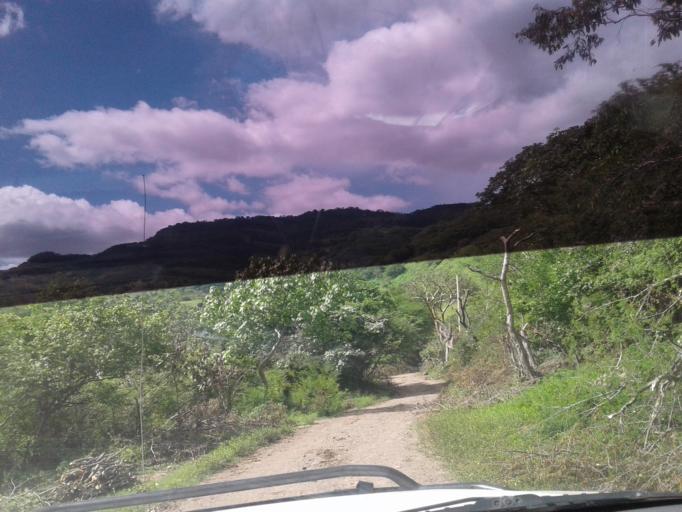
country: NI
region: Leon
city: Santa Rosa del Penon
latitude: 12.8735
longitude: -86.2428
